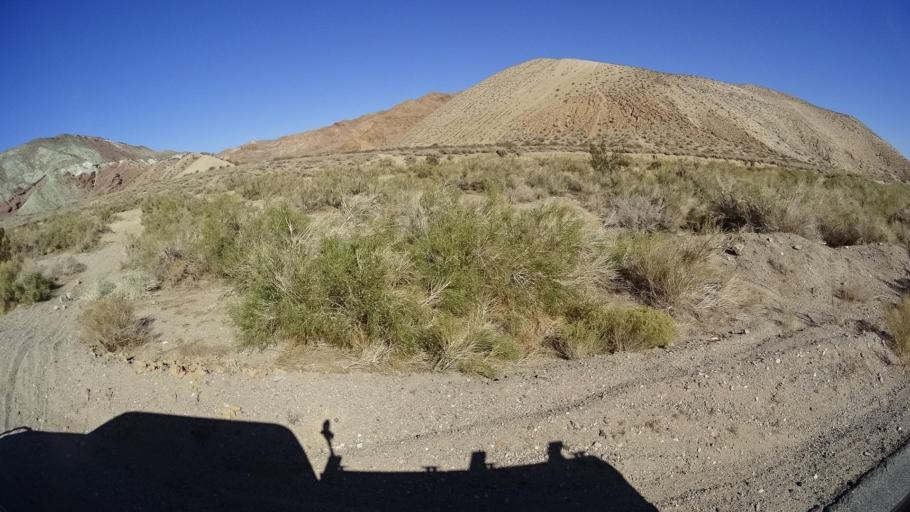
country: US
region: California
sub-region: Kern County
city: California City
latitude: 35.3172
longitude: -118.0779
